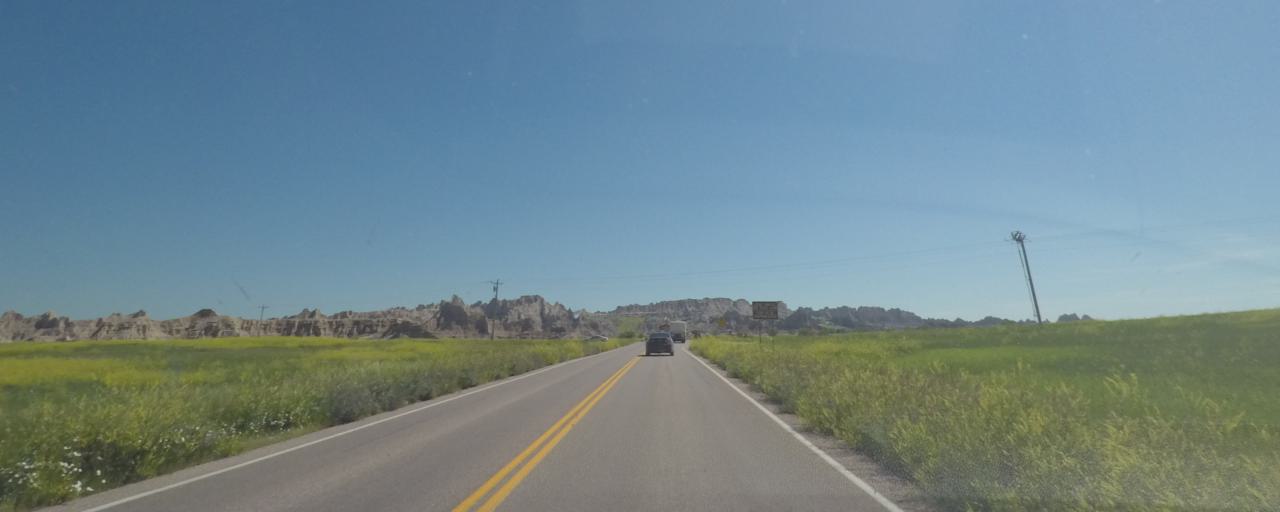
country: US
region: South Dakota
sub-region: Haakon County
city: Philip
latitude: 43.7417
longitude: -101.9579
